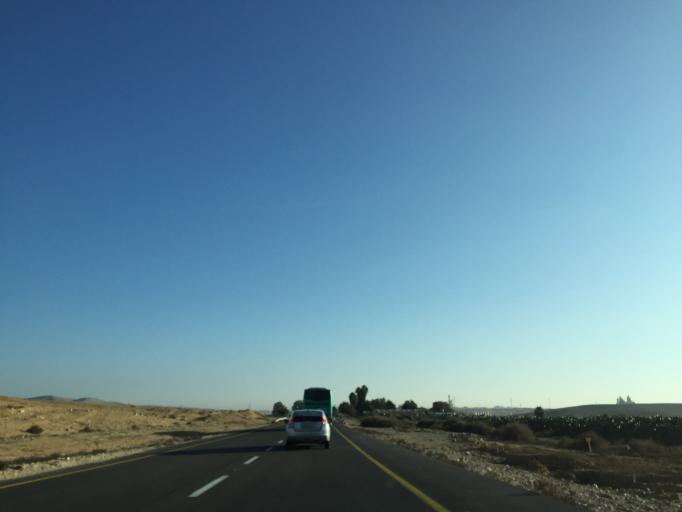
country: IL
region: Southern District
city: Dimona
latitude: 31.0515
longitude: 34.9936
